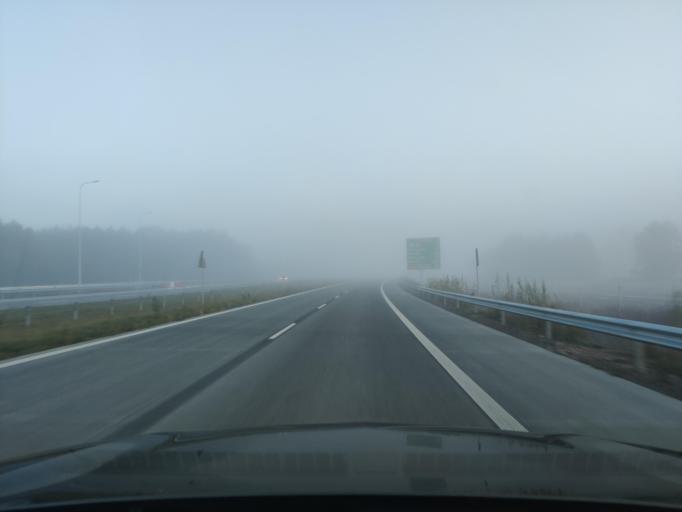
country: PL
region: Masovian Voivodeship
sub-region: Powiat ciechanowski
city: Glinojeck
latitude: 52.8239
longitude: 20.2618
